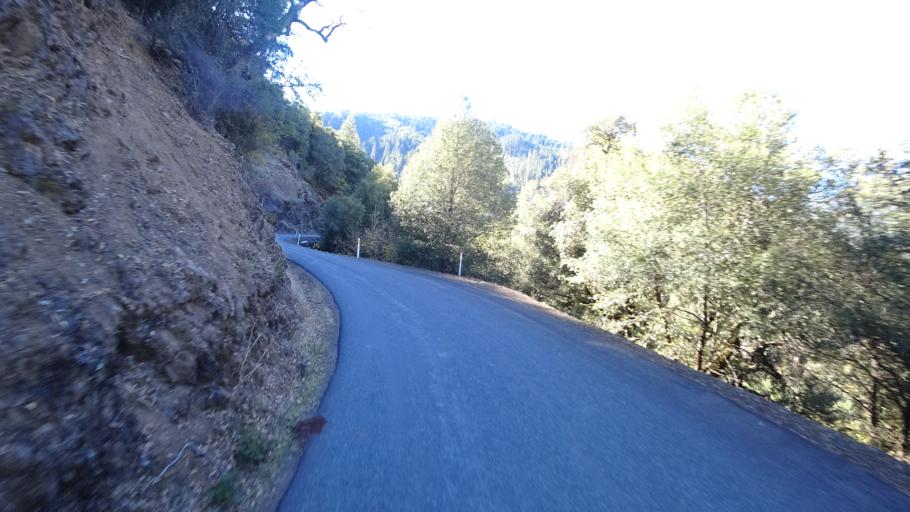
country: US
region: California
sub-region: Humboldt County
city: Willow Creek
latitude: 41.1509
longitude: -123.2095
